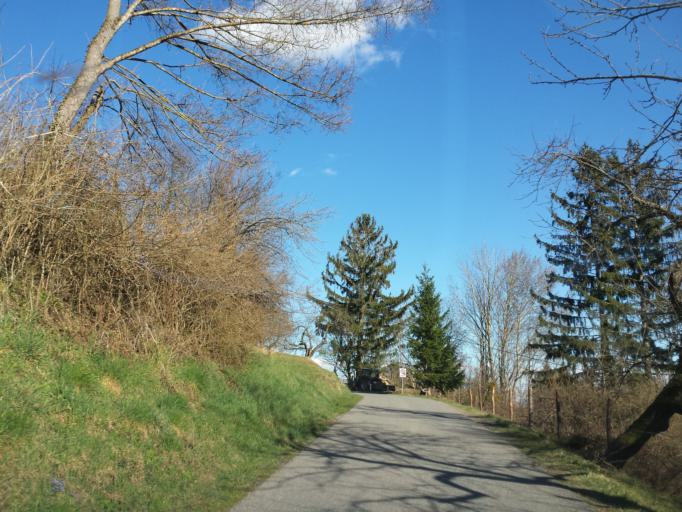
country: AT
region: Styria
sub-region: Politischer Bezirk Graz-Umgebung
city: Sankt Radegund bei Graz
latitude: 47.1681
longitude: 15.4767
